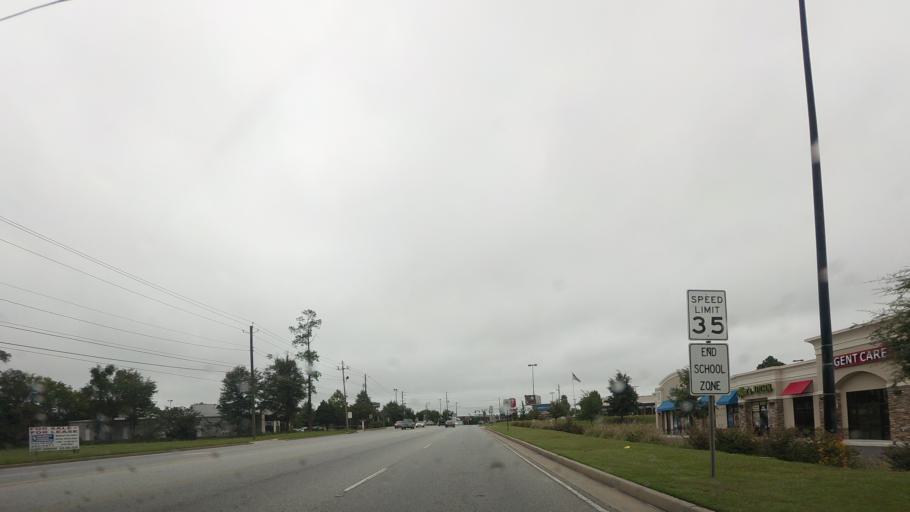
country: US
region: Georgia
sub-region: Lowndes County
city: Remerton
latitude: 30.8381
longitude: -83.3208
